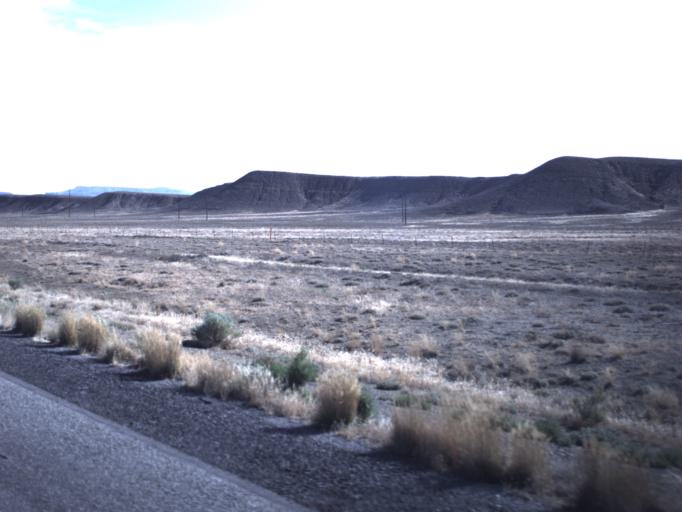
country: US
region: Utah
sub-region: Grand County
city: Moab
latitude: 38.7898
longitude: -109.7563
